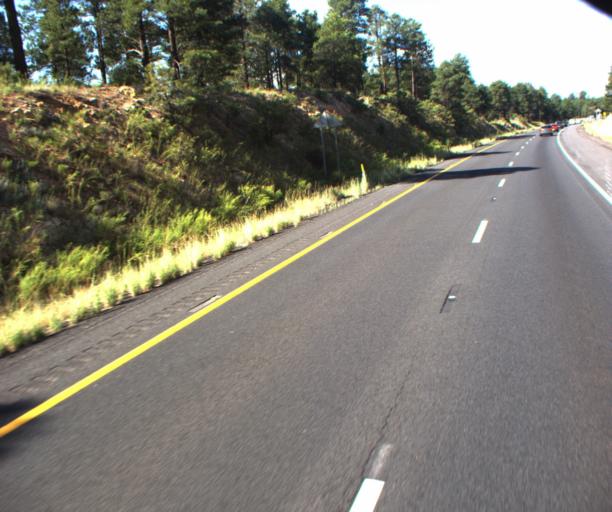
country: US
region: Arizona
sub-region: Coconino County
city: Flagstaff
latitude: 35.1757
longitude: -111.6441
